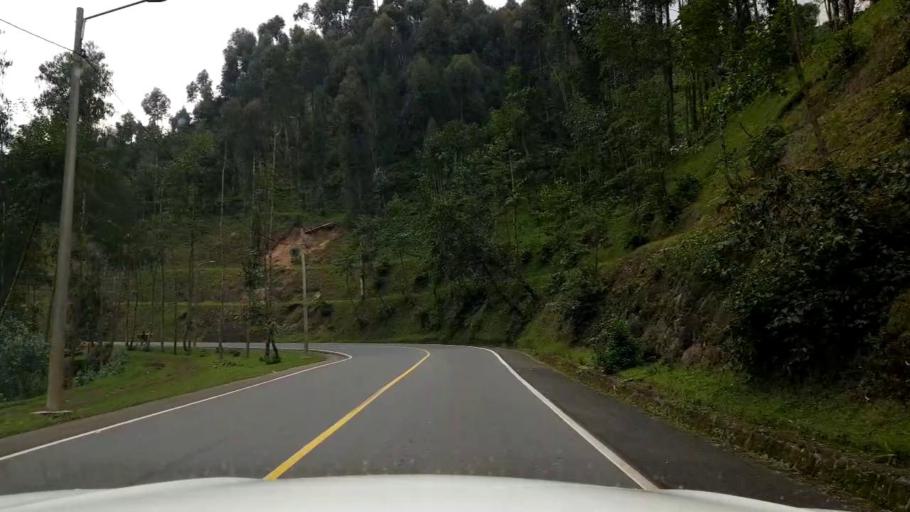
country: RW
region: Northern Province
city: Musanze
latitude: -1.6164
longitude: 29.4953
